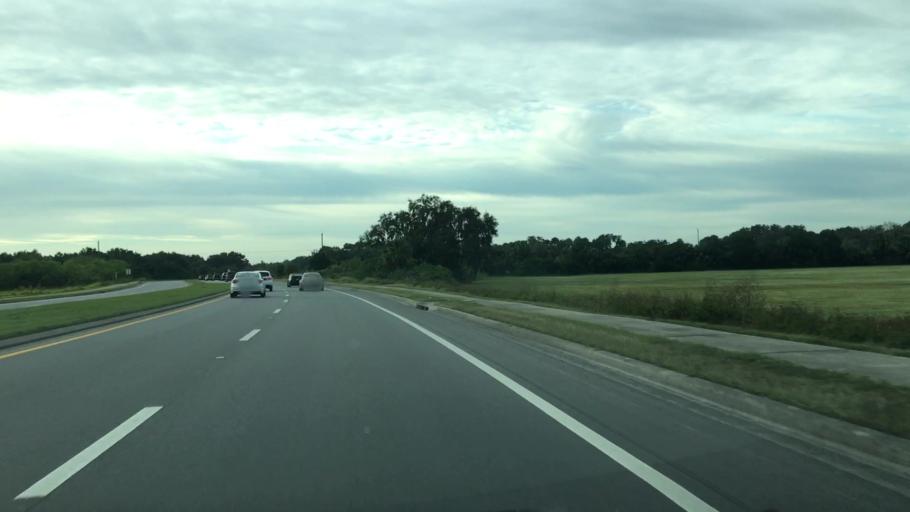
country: US
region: Florida
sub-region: Seminole County
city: Midway
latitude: 28.7753
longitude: -81.2104
